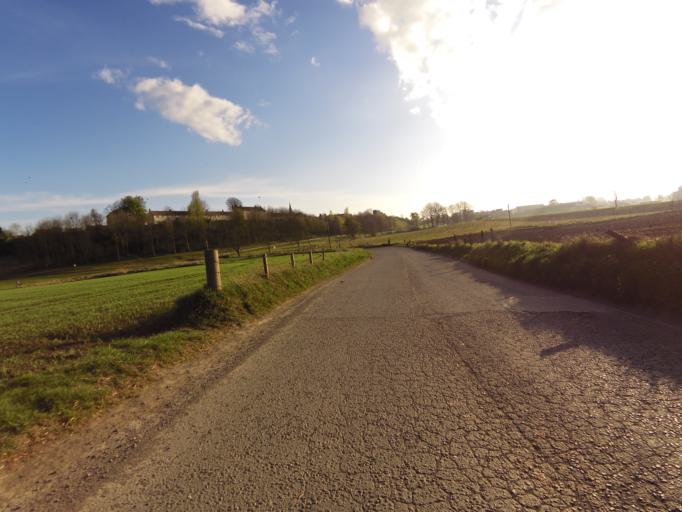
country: GB
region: Scotland
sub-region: Fife
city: Leslie
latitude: 56.2057
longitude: -3.2071
